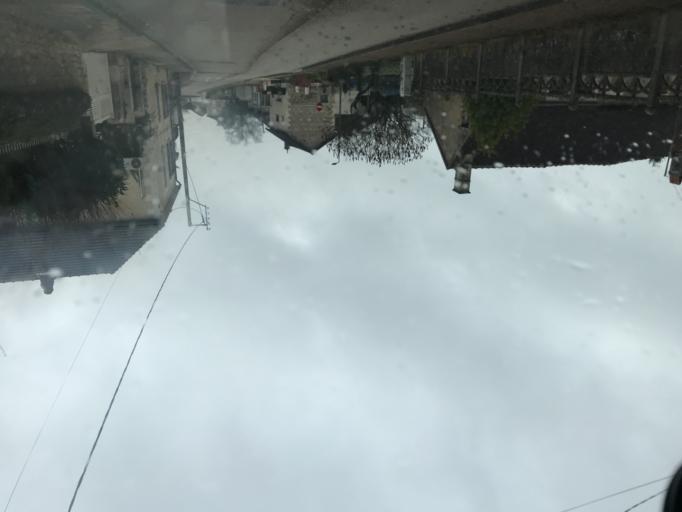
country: FR
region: Bourgogne
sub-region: Departement de l'Yonne
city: Fontenailles
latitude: 47.6127
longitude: 3.4988
